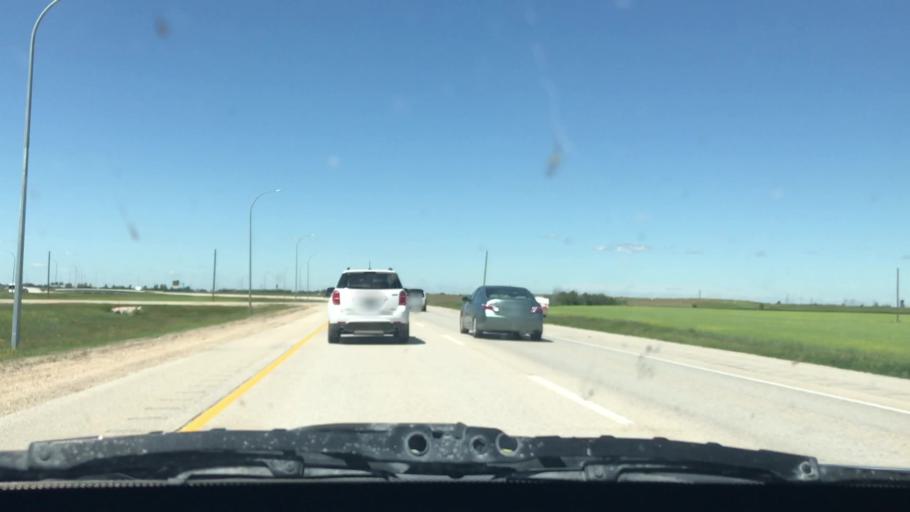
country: CA
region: Manitoba
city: Winnipeg
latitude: 49.8255
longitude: -96.9458
